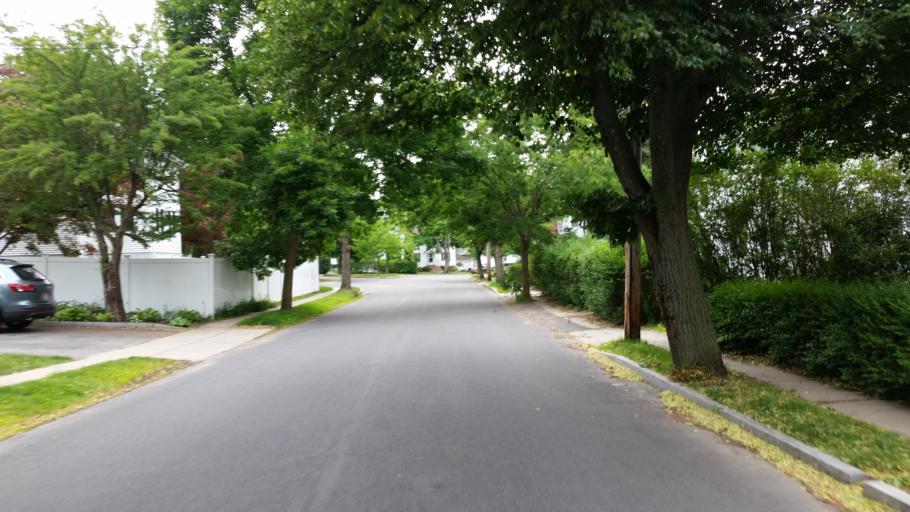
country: US
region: Massachusetts
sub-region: Middlesex County
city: Belmont
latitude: 42.3899
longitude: -71.1772
